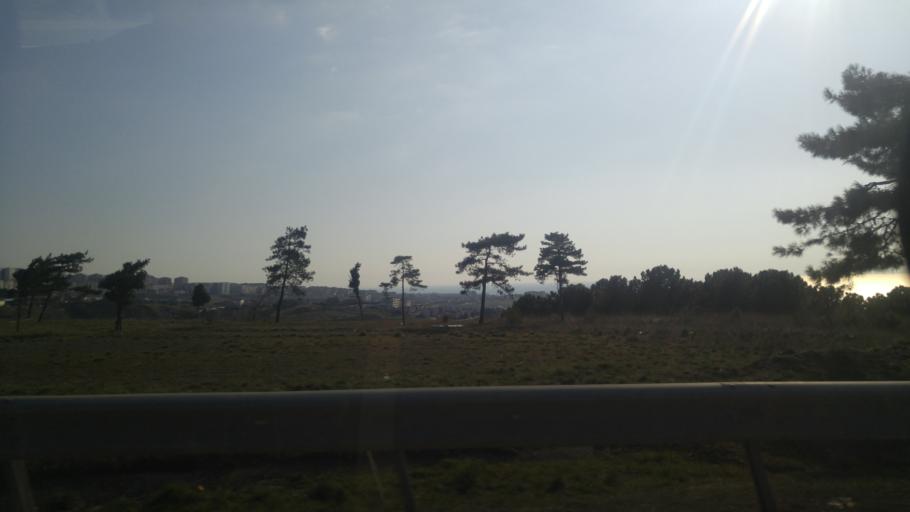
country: TR
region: Istanbul
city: Gurpinar
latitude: 41.0258
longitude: 28.6182
